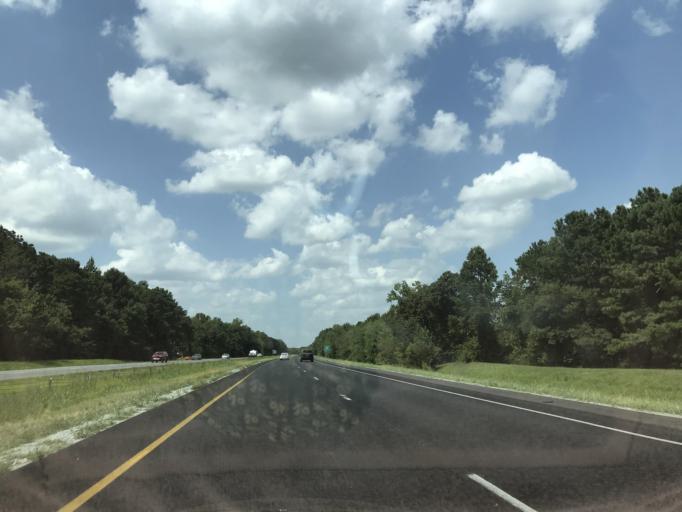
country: US
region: North Carolina
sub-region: Duplin County
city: Warsaw
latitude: 34.9357
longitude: -78.0504
